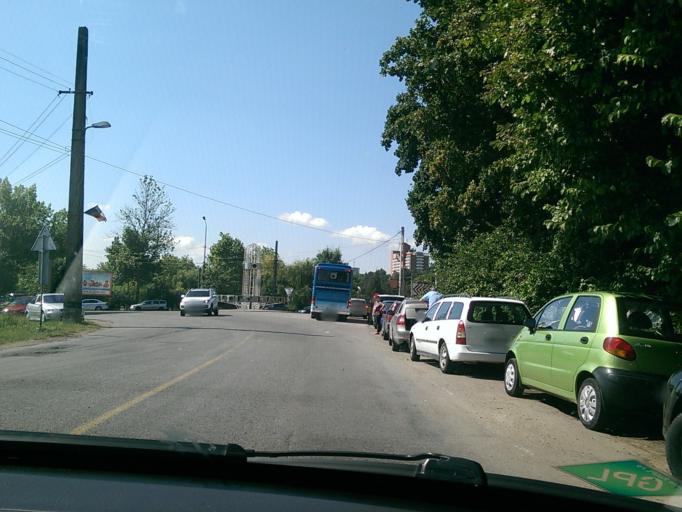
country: RO
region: Bihor
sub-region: Comuna Sanmartin
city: Sanmartin
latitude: 46.9971
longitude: 21.9791
